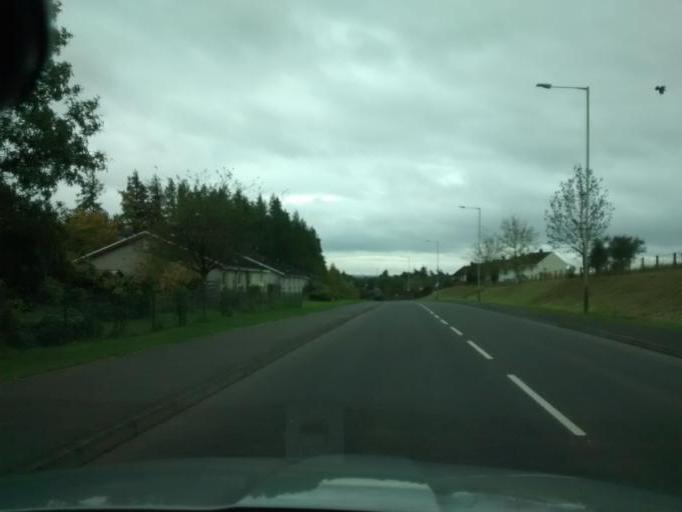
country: GB
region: Scotland
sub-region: Perth and Kinross
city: Blairgowrie
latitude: 56.5780
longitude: -3.3465
